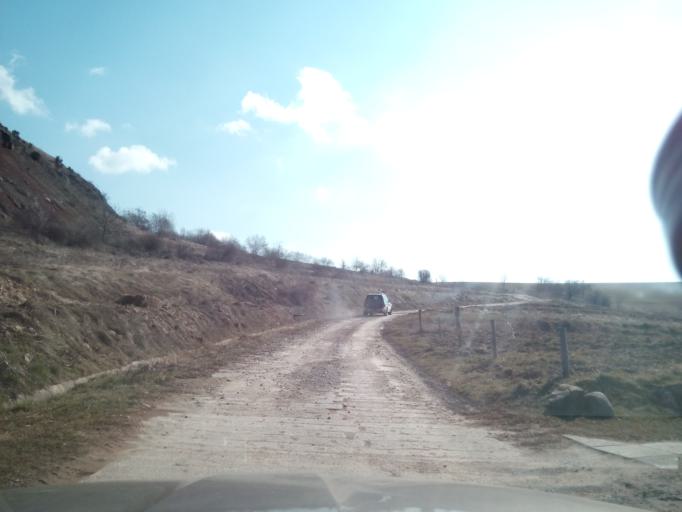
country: SK
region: Presovsky
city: Lipany
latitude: 49.1934
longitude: 20.9661
